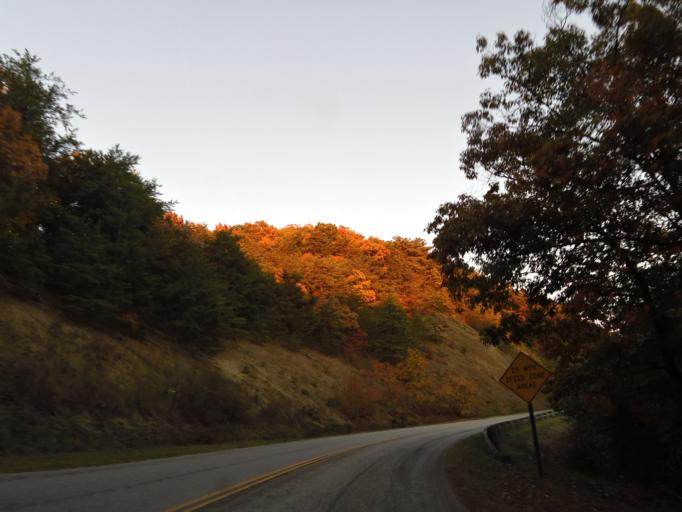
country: US
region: Tennessee
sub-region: Blount County
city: Maryville
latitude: 35.6319
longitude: -83.9458
